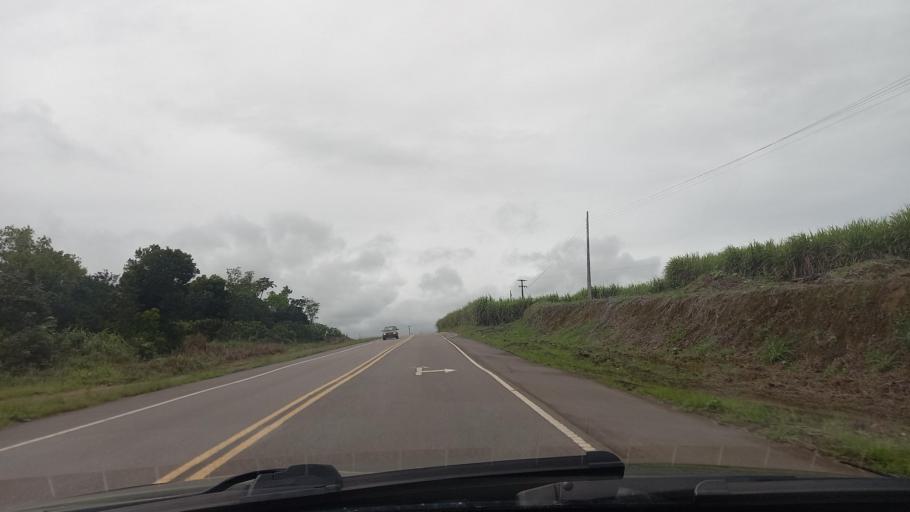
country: BR
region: Alagoas
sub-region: Sao Miguel Dos Campos
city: Sao Miguel dos Campos
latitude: -9.8044
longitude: -36.2031
